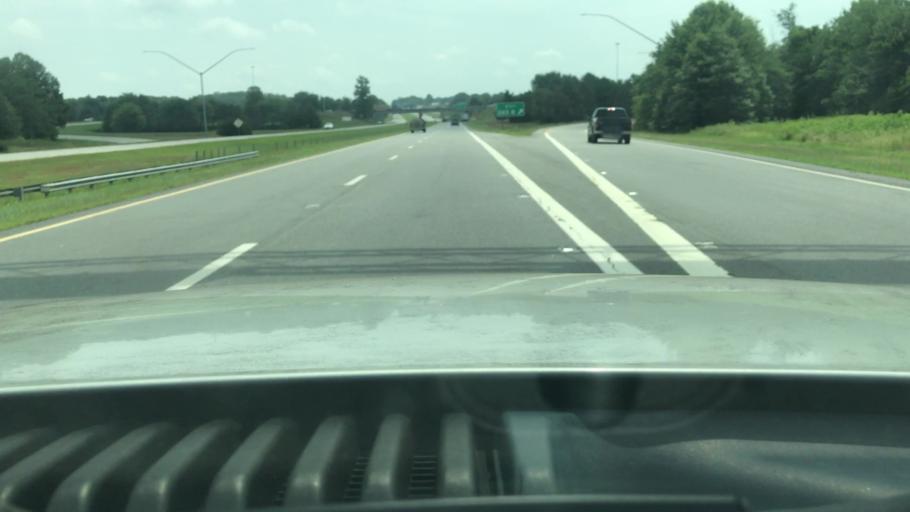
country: US
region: North Carolina
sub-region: Yadkin County
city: Jonesville
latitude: 36.1232
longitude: -80.8191
